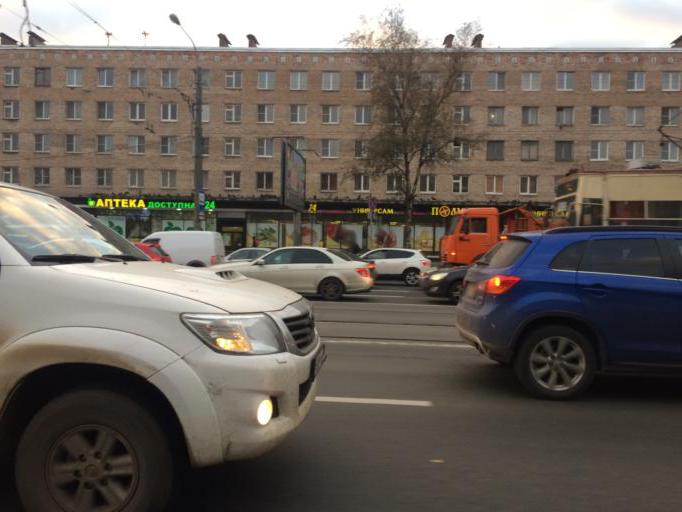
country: RU
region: St.-Petersburg
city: Obukhovo
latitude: 59.8816
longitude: 30.4683
